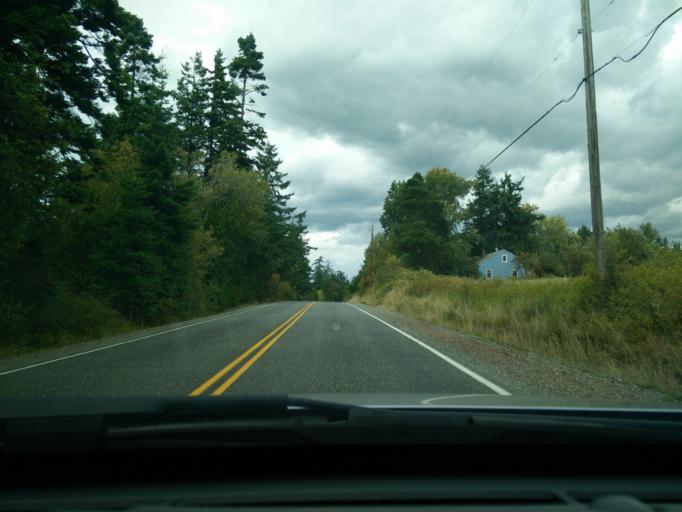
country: US
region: Washington
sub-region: Skagit County
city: Anacortes
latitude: 48.5018
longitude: -122.4819
